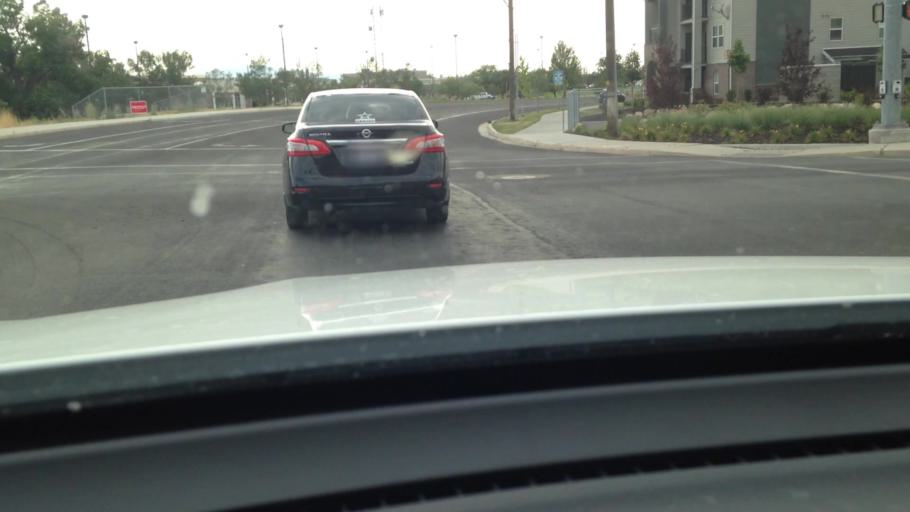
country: US
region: Utah
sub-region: Davis County
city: Farmington
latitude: 40.9806
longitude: -111.9014
